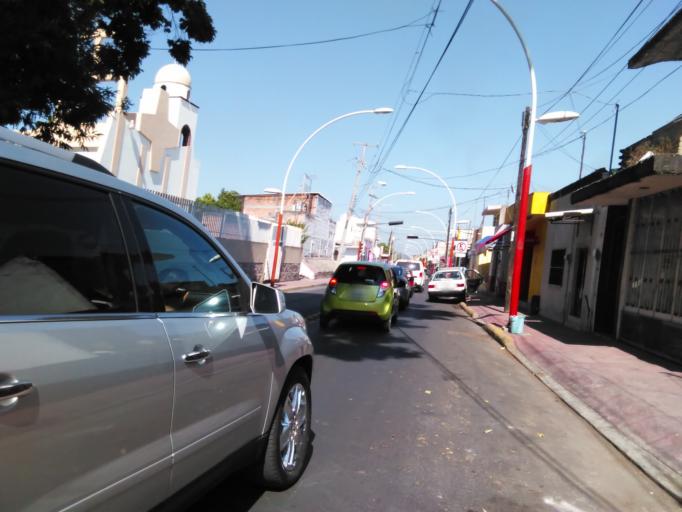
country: MX
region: Nayarit
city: Tepic
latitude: 21.4960
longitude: -104.8896
